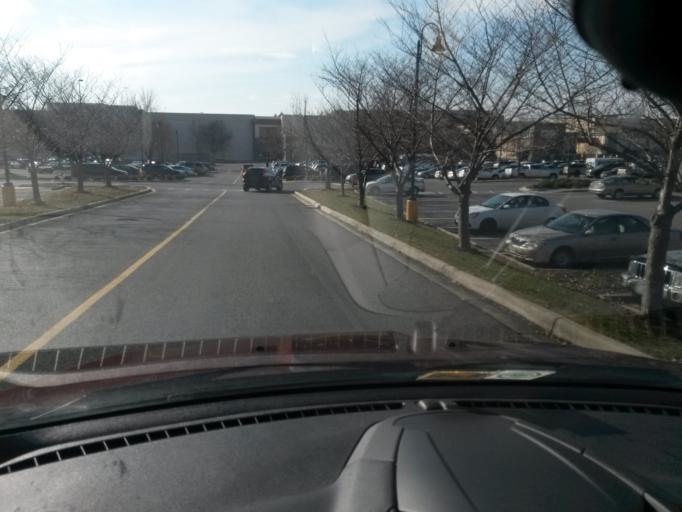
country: US
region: Virginia
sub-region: City of Roanoke
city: Roanoke
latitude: 37.3047
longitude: -79.9615
